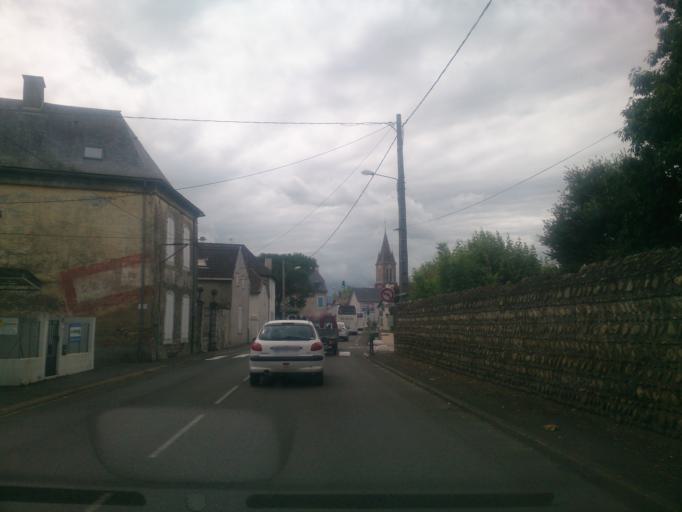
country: FR
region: Midi-Pyrenees
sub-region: Departement des Hautes-Pyrenees
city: Laloubere
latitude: 43.2083
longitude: 0.0732
